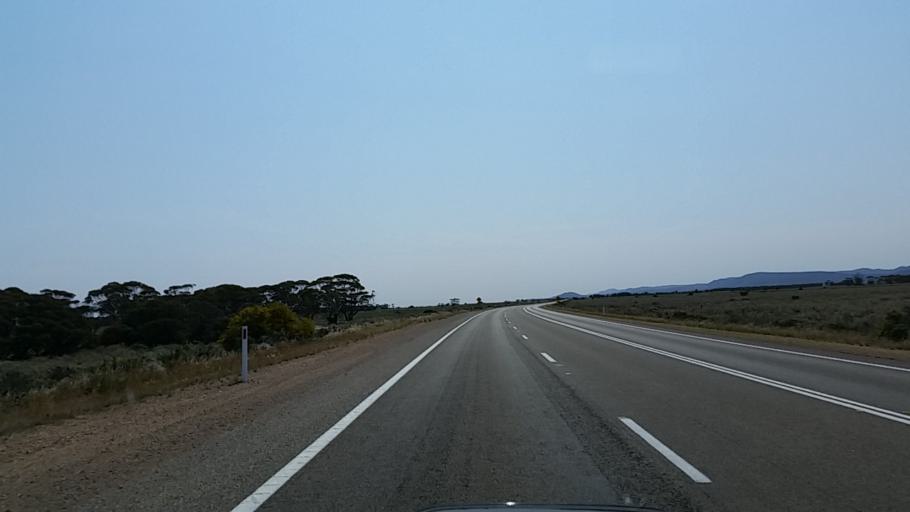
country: AU
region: South Australia
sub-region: Port Pirie City and Dists
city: Port Pirie
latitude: -32.9750
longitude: 137.9828
